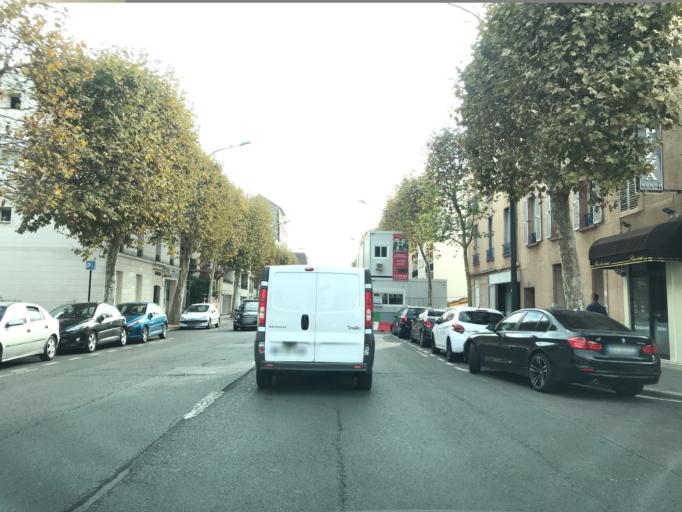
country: FR
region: Ile-de-France
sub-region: Departement des Hauts-de-Seine
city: La Garenne-Colombes
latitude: 48.9061
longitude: 2.2508
